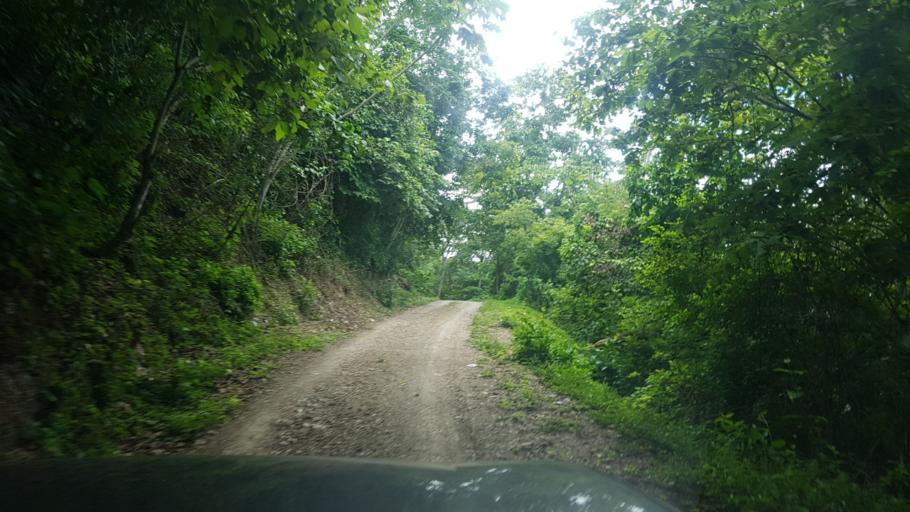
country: NI
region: Nueva Segovia
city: Mozonte
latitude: 13.5955
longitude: -86.4178
